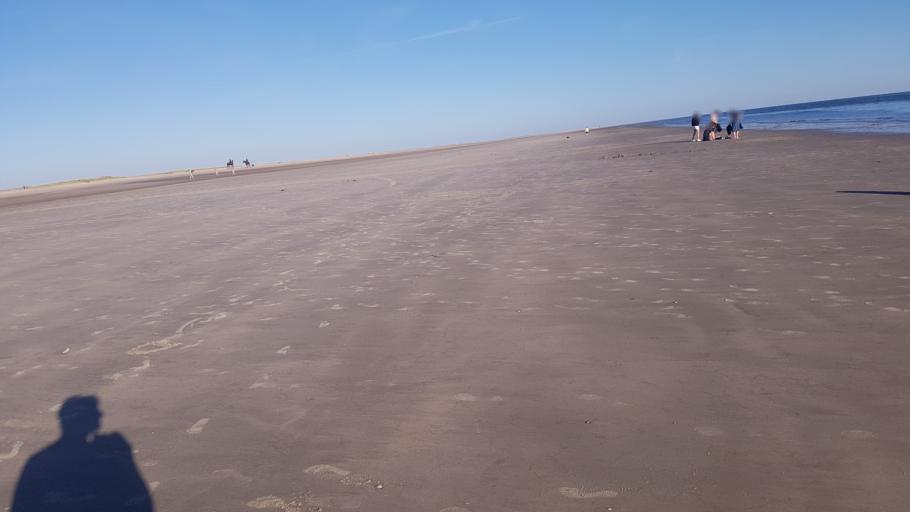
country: DE
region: Schleswig-Holstein
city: List
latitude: 55.0727
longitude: 8.4883
